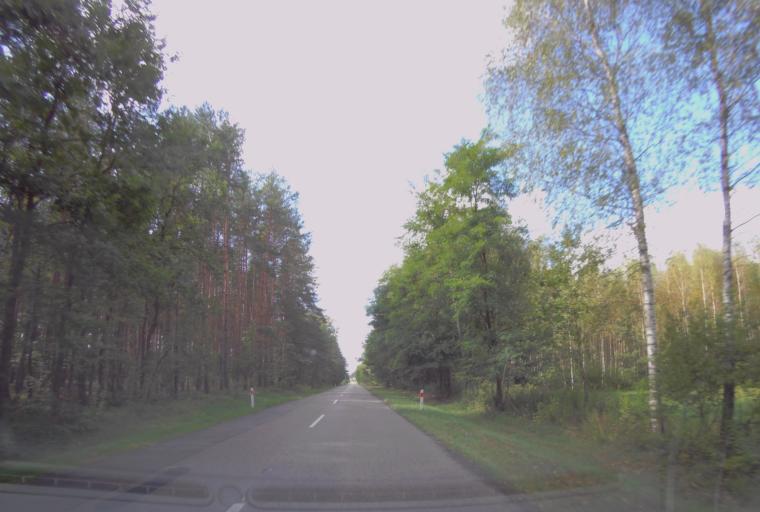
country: PL
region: Subcarpathian Voivodeship
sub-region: Powiat stalowowolski
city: Bojanow
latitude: 50.3969
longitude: 22.0152
